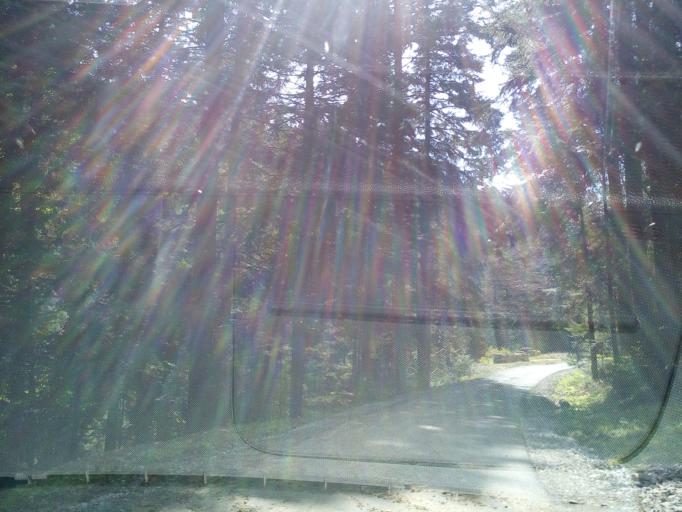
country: PL
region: Lesser Poland Voivodeship
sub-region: Powiat nowosadecki
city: Labowa
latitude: 49.4664
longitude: 20.8586
